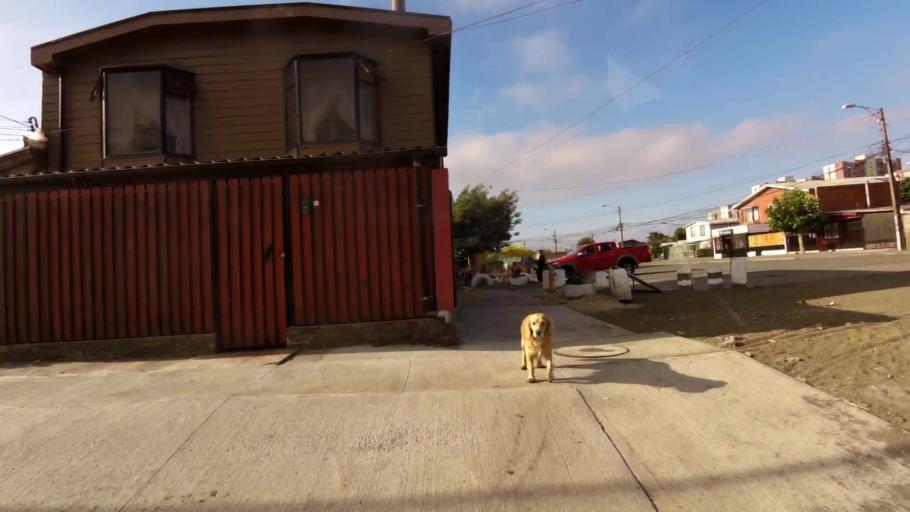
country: CL
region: Biobio
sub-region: Provincia de Concepcion
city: Concepcion
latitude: -36.7902
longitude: -73.0932
